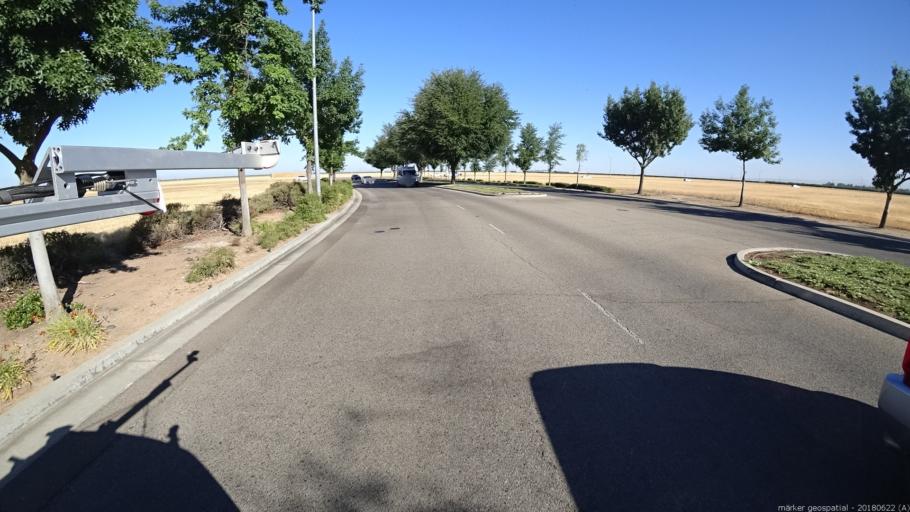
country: US
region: California
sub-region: Fresno County
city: Clovis
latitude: 36.8873
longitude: -119.8034
